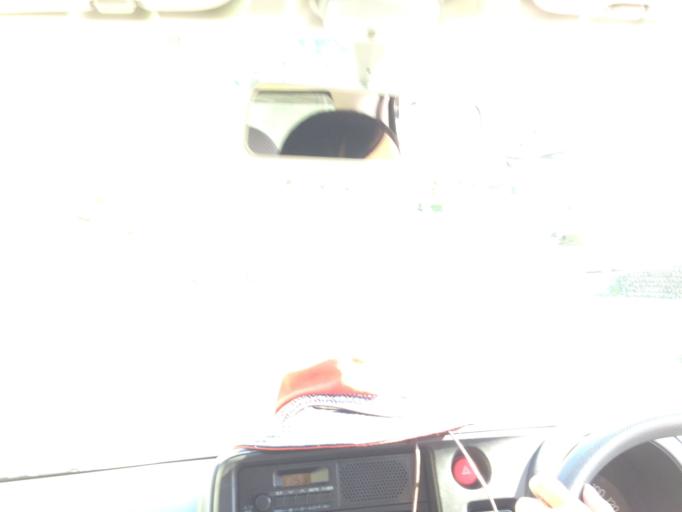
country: JP
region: Gifu
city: Mitake
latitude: 35.6124
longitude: 137.1839
